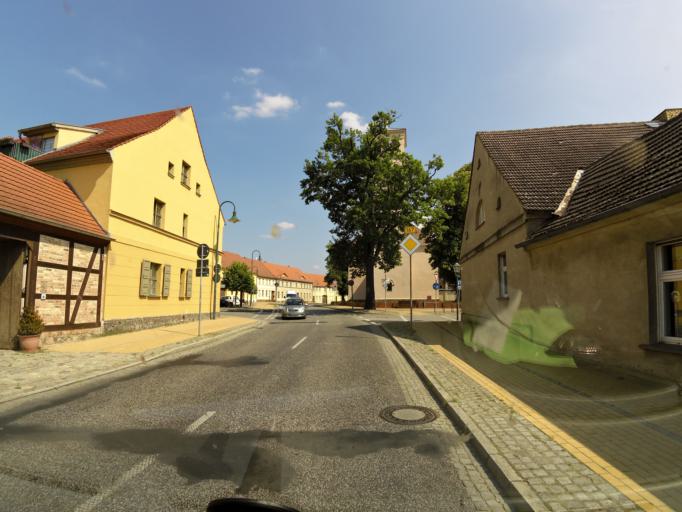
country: DE
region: Brandenburg
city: Liebenwalde
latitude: 52.8714
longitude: 13.3887
